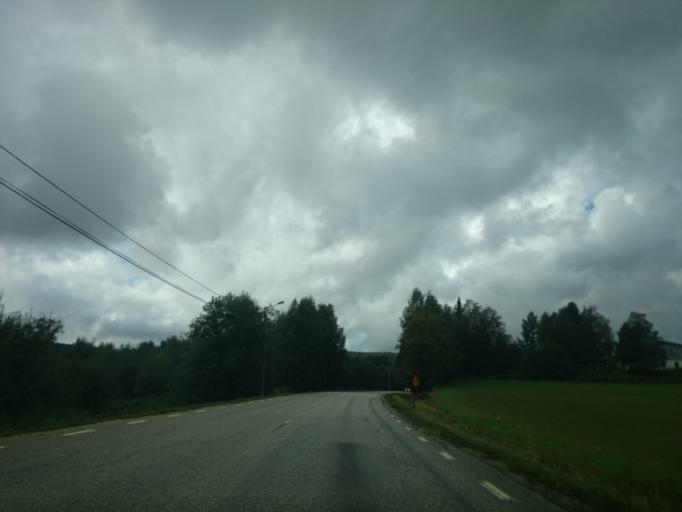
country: SE
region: Vaesternorrland
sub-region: Sundsvalls Kommun
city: Vi
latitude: 62.3114
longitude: 17.1952
